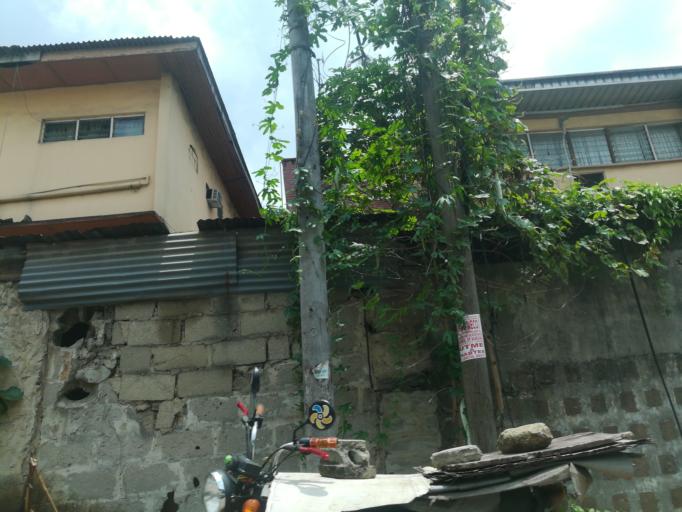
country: NG
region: Lagos
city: Somolu
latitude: 6.5512
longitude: 3.3661
